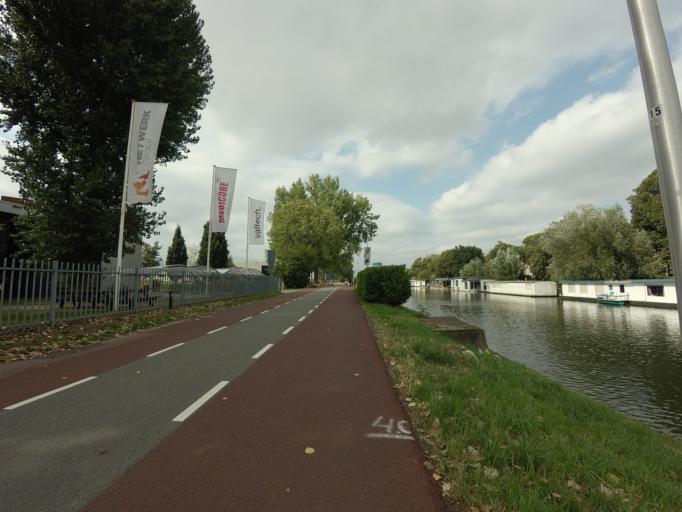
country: NL
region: Utrecht
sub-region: Gemeente Utrecht
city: Utrecht
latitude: 52.0708
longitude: 5.1108
